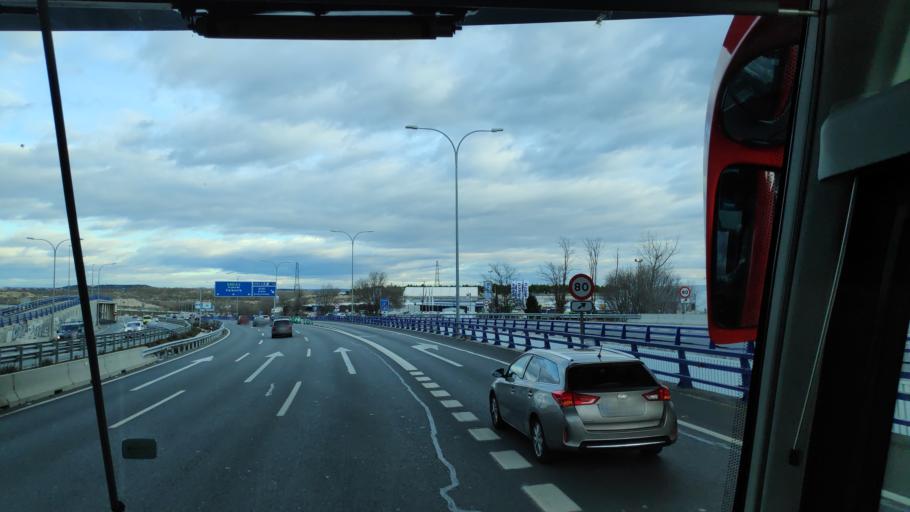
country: ES
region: Madrid
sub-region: Provincia de Madrid
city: Villa de Vallecas
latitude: 40.3675
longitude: -3.5848
